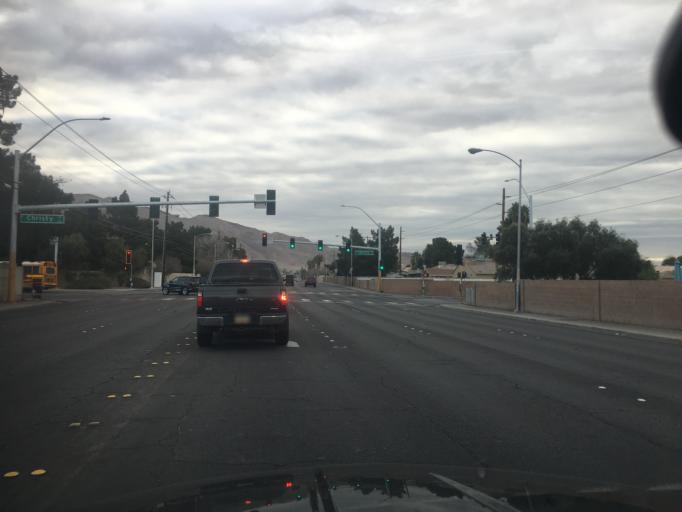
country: US
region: Nevada
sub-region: Clark County
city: Sunrise Manor
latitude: 36.1594
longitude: -115.0540
